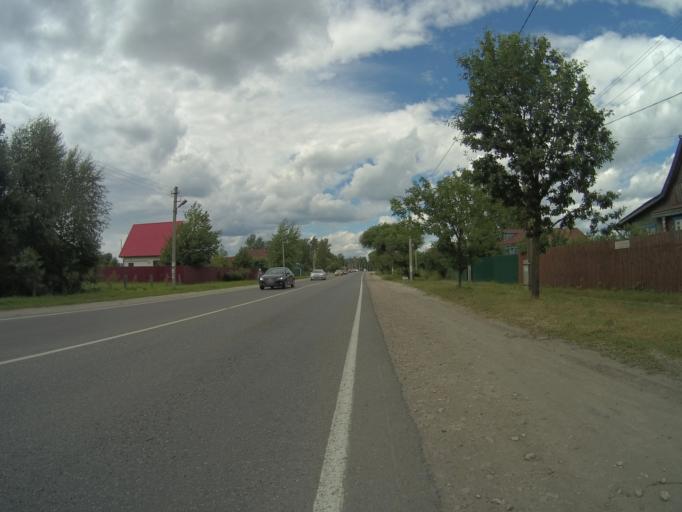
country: RU
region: Vladimir
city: Kommunar
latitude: 56.0445
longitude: 40.5413
